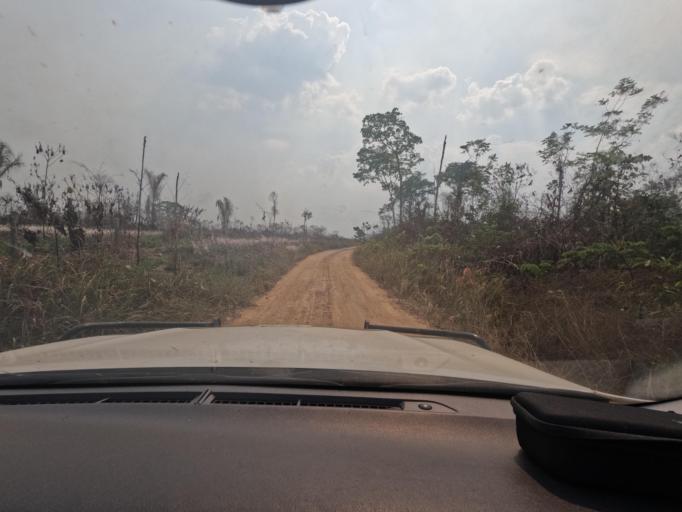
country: BR
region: Rondonia
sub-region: Porto Velho
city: Porto Velho
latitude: -8.7729
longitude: -63.2072
